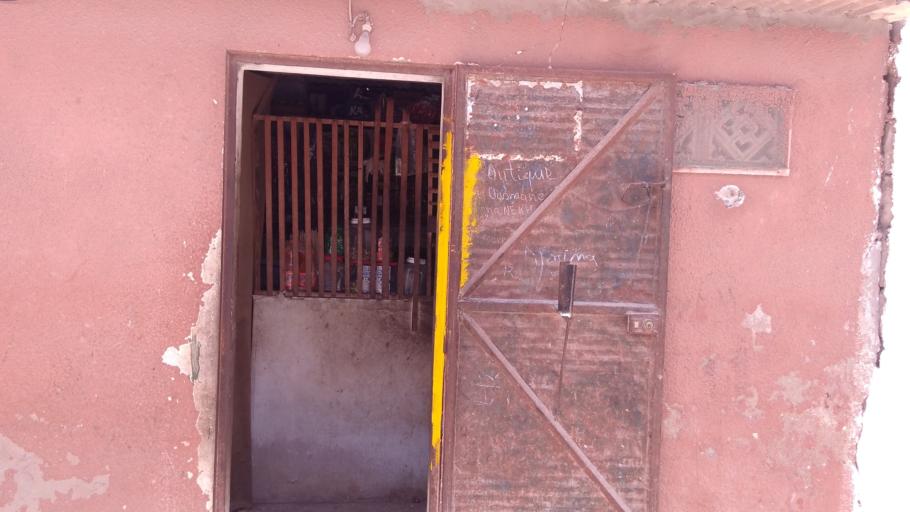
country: SN
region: Dakar
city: Pikine
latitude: 14.6858
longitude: -17.2264
